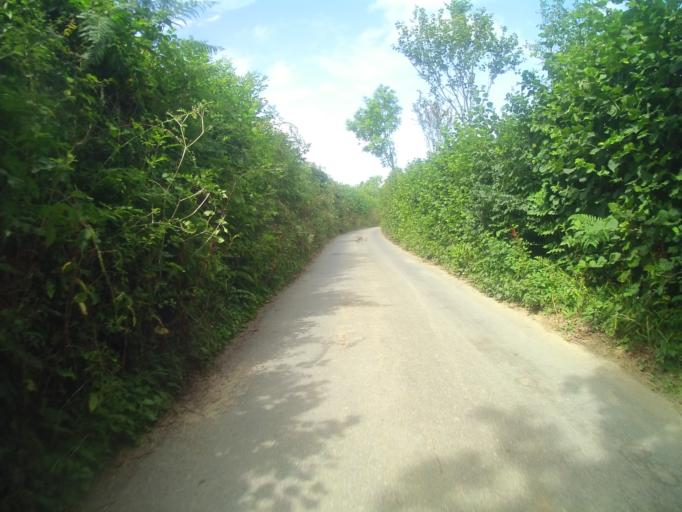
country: GB
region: England
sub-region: Devon
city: Buckfastleigh
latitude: 50.4929
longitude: -3.7899
